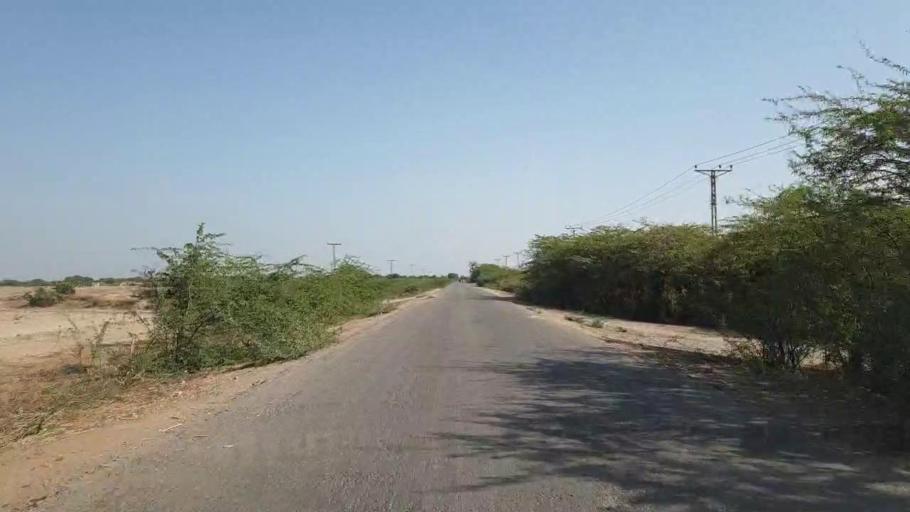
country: PK
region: Sindh
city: Umarkot
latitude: 25.4289
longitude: 69.7414
